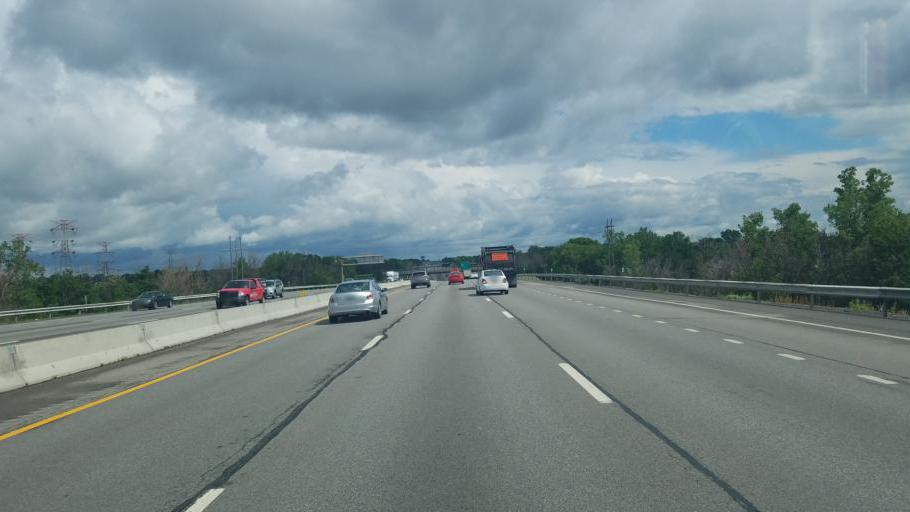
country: US
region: New York
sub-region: Erie County
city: Cheektowaga
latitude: 42.9152
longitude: -78.7663
